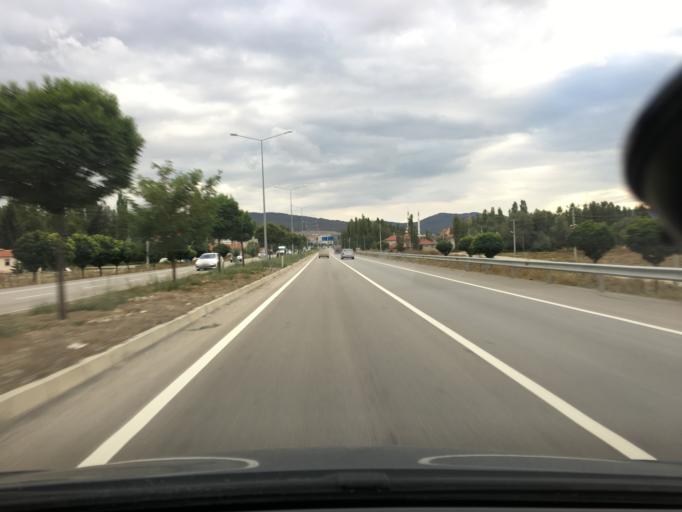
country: TR
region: Afyonkarahisar
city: Sincanli
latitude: 38.7359
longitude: 30.3492
